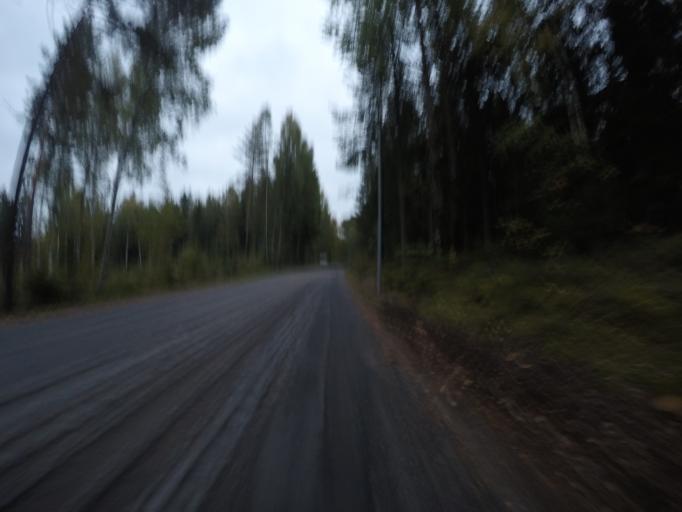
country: SE
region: Vaestmanland
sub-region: Kungsors Kommun
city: Kungsoer
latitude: 59.3932
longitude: 16.1144
